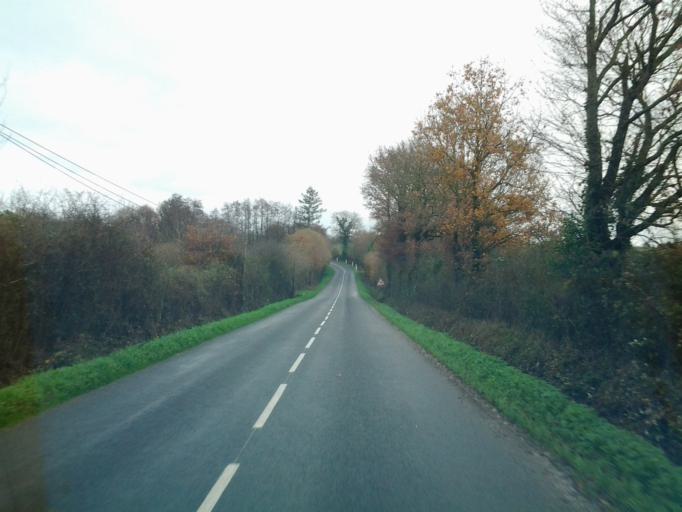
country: FR
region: Pays de la Loire
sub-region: Departement de la Vendee
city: Bournezeau
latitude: 46.6234
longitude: -1.1982
